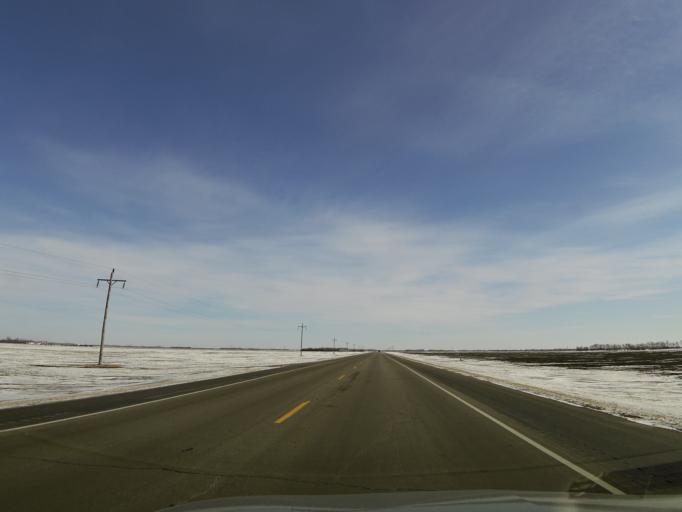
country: US
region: North Dakota
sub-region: Walsh County
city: Grafton
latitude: 48.4123
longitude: -97.2925
